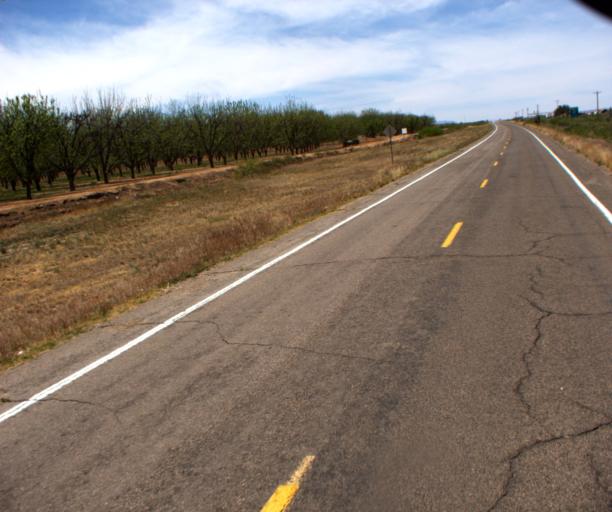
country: US
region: Arizona
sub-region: Cochise County
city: Willcox
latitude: 32.3285
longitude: -109.4967
